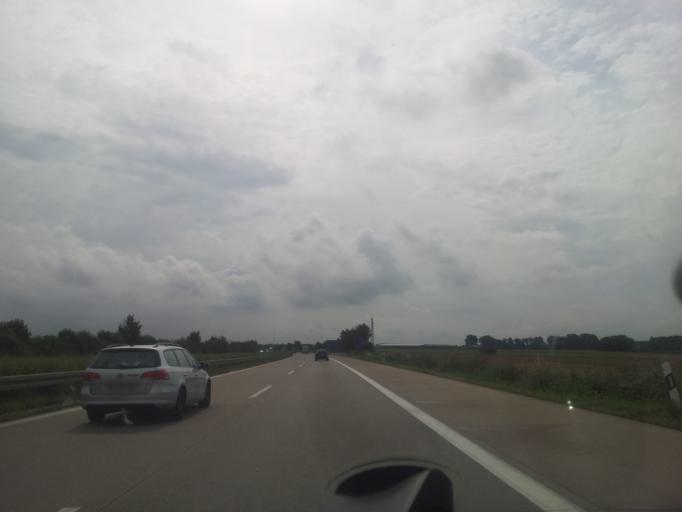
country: DE
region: Saxony-Anhalt
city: Nauendorf
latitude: 51.5791
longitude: 11.8888
